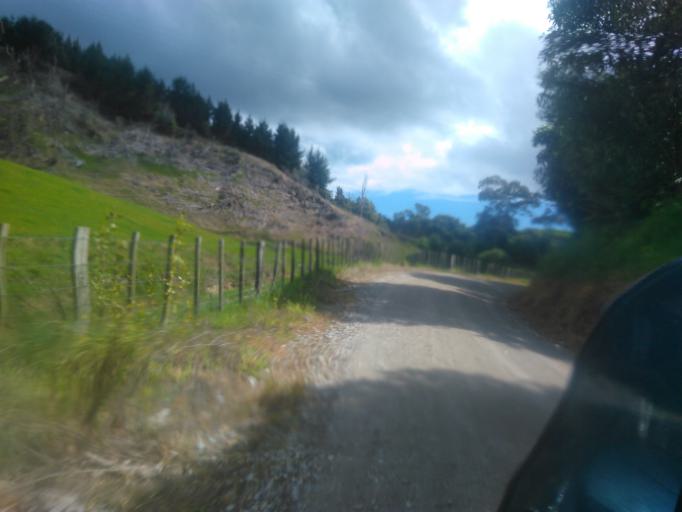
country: NZ
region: Hawke's Bay
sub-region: Wairoa District
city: Wairoa
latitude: -38.7620
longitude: 177.5927
